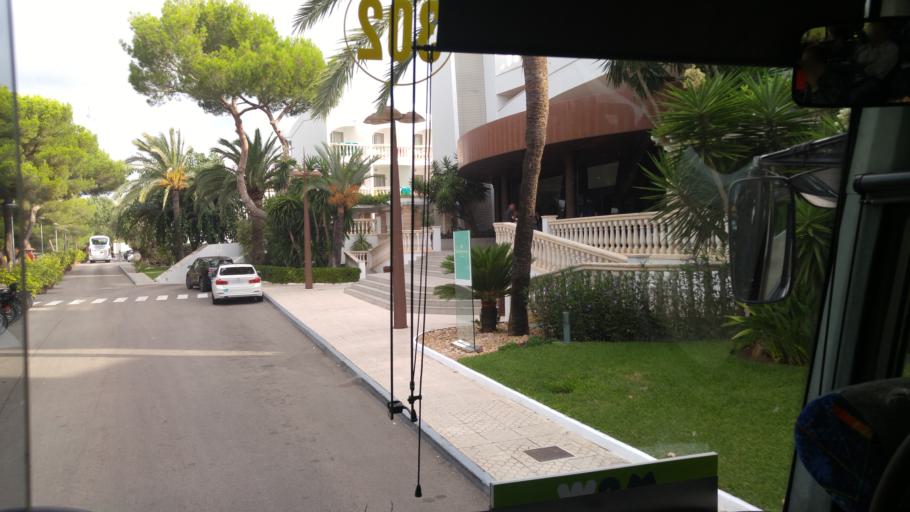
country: ES
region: Balearic Islands
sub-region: Illes Balears
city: Port d'Alcudia
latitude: 39.7865
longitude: 3.1280
